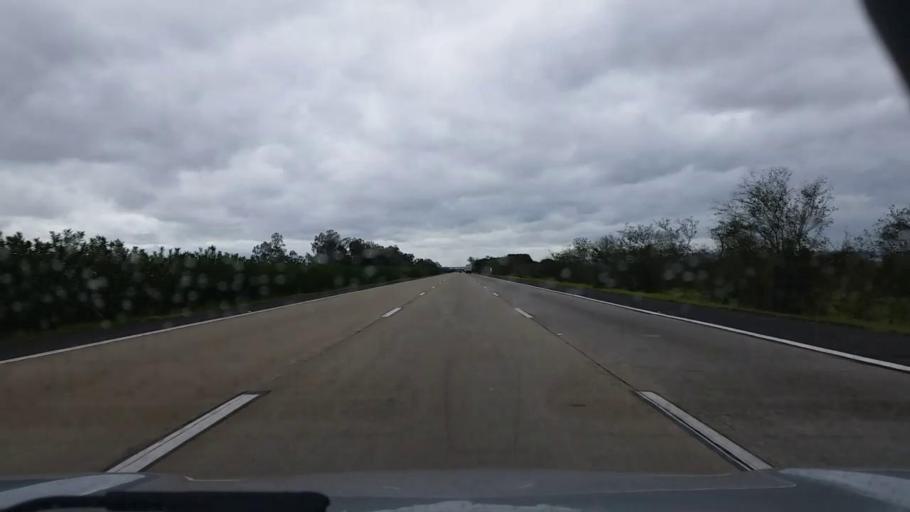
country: BR
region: Rio Grande do Sul
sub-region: Rolante
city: Rolante
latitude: -29.8863
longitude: -50.6425
